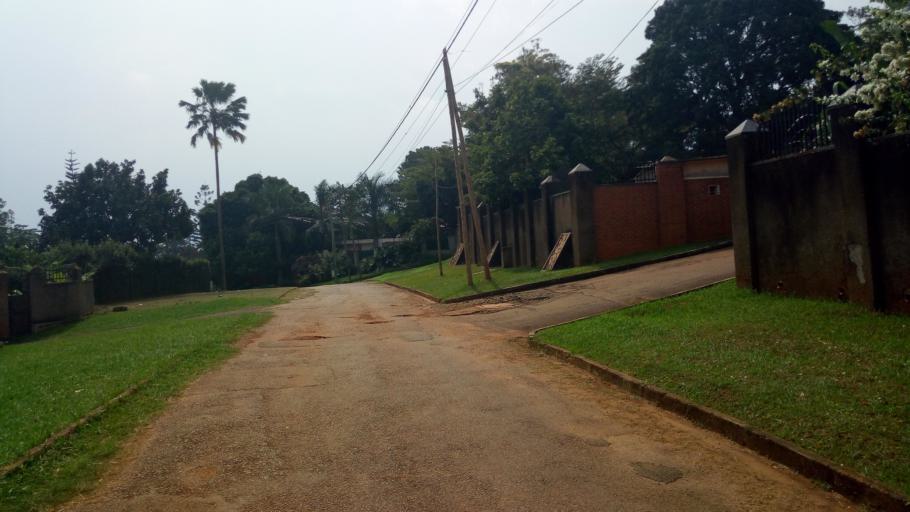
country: UG
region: Central Region
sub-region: Kampala District
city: Kampala
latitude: 0.3126
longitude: 32.6206
